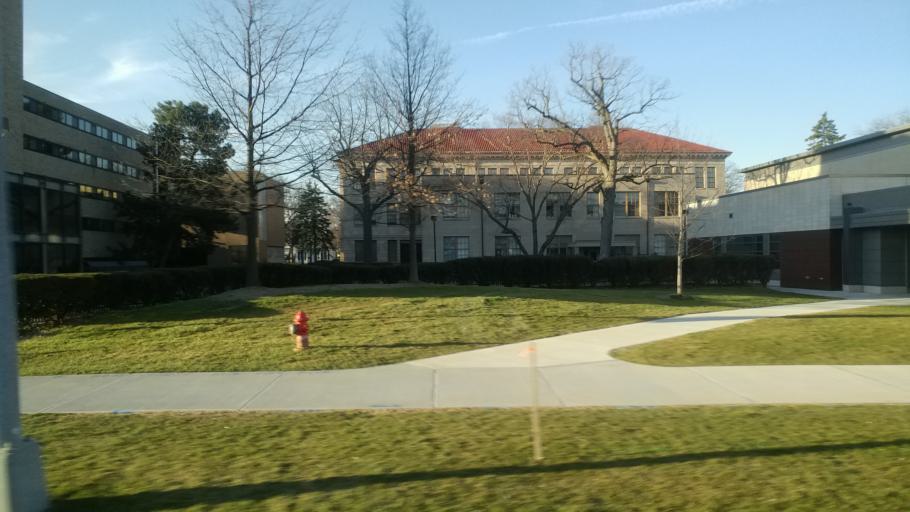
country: US
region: Ohio
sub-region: Wood County
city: Bowling Green
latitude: 41.3748
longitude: -83.6411
